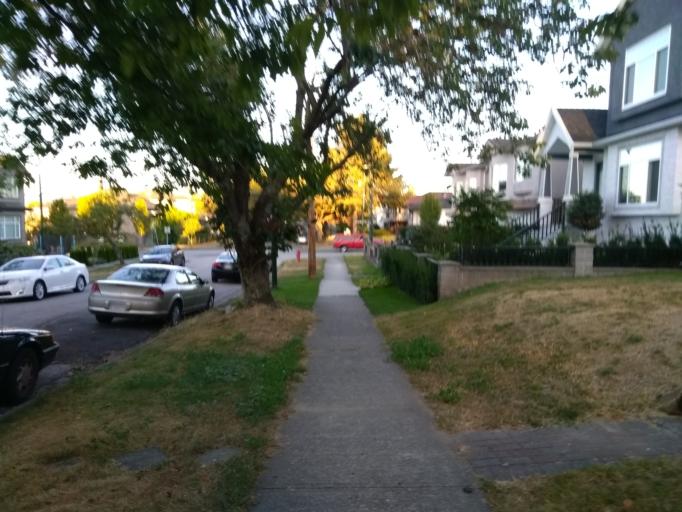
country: CA
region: British Columbia
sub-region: Fraser Valley Regional District
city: North Vancouver
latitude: 49.2462
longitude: -123.0424
